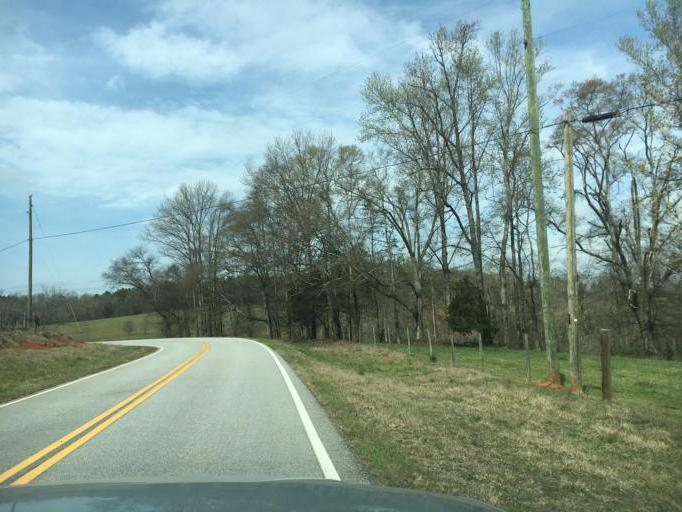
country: US
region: Georgia
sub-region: Franklin County
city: Lavonia
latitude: 34.4319
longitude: -83.0466
